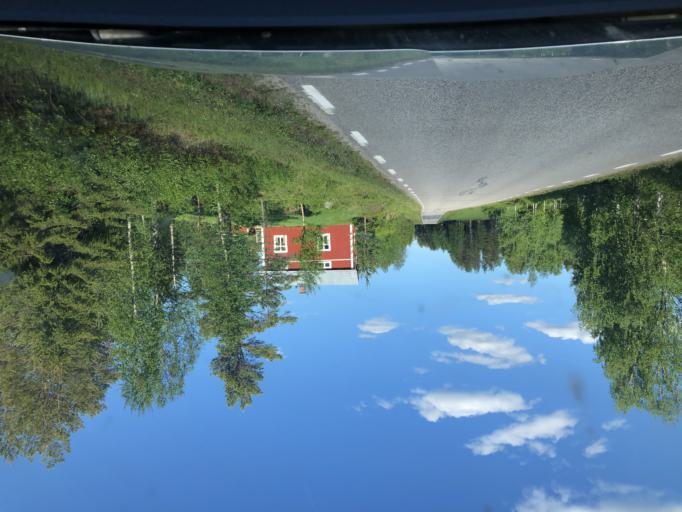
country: SE
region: Norrbotten
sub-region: Kalix Kommun
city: Kalix
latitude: 66.0871
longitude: 23.2182
